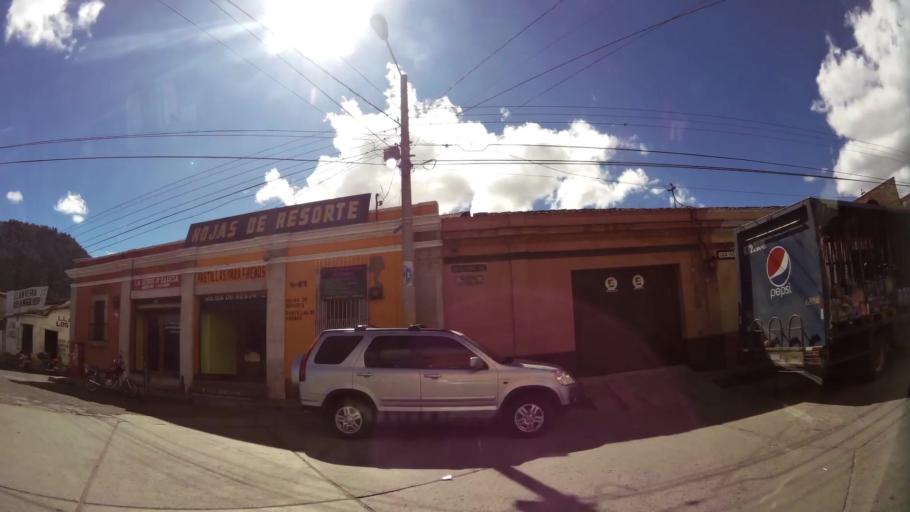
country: GT
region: Quetzaltenango
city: Quetzaltenango
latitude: 14.8338
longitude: -91.5136
